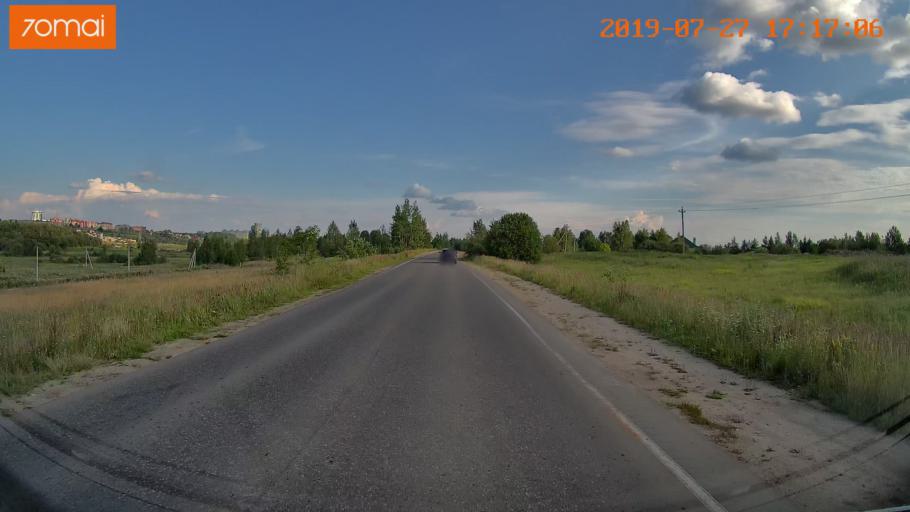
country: RU
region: Ivanovo
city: Novo-Talitsy
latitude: 57.0403
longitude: 40.8917
